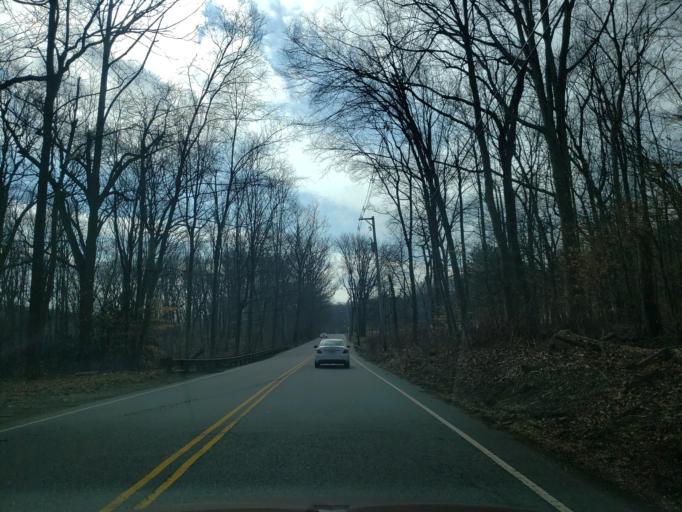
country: US
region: New Jersey
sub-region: Essex County
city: Short Hills
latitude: 40.7458
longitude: -74.3014
